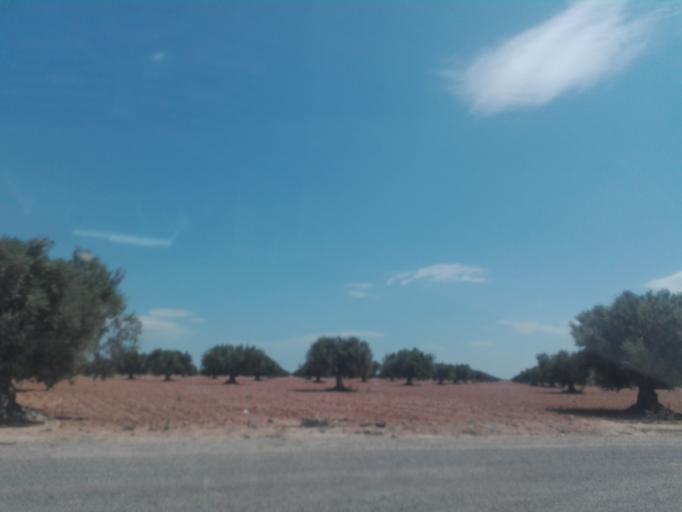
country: TN
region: Safaqis
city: Sfax
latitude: 34.6704
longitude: 10.5733
